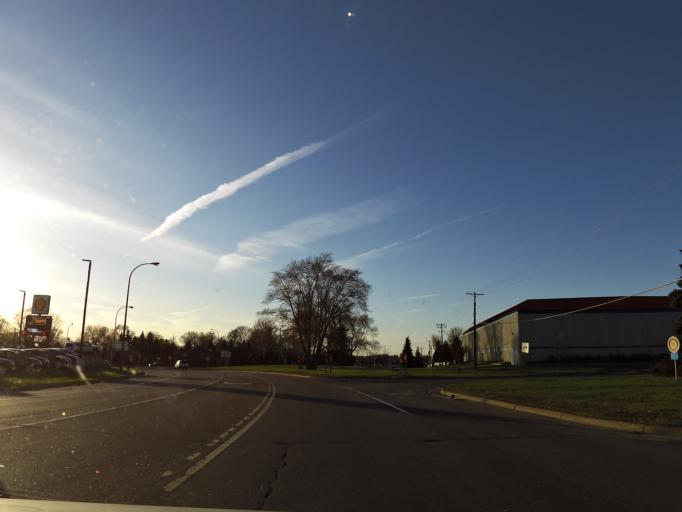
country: US
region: Minnesota
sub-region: Dakota County
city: Hastings
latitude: 44.7186
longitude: -92.8480
